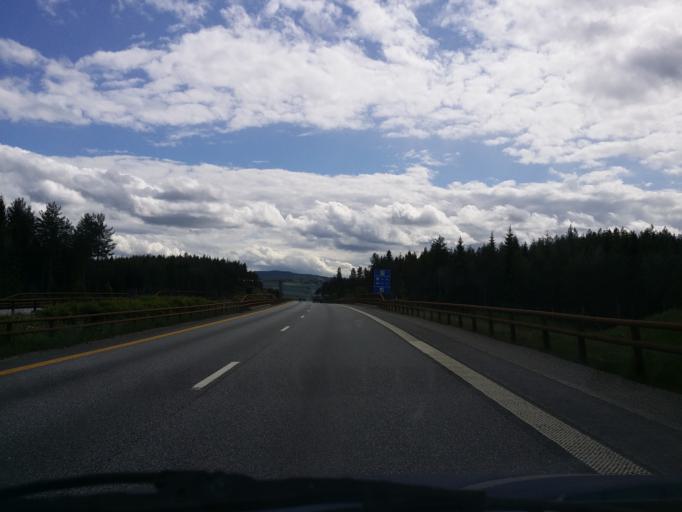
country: NO
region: Hedmark
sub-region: Stange
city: Stange
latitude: 60.6513
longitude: 11.2919
